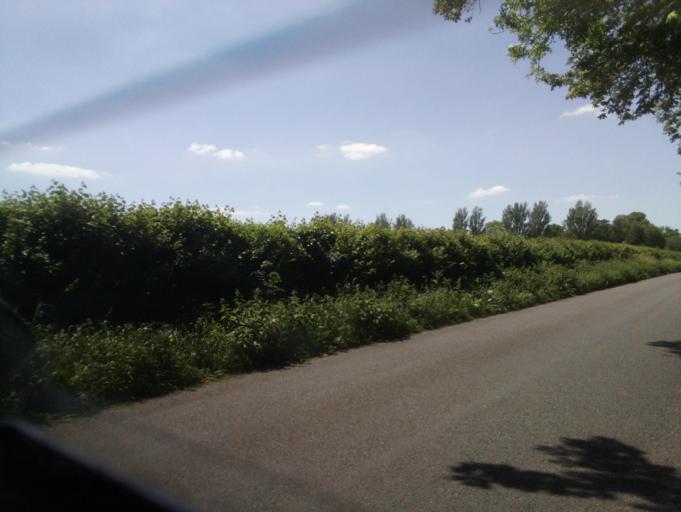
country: GB
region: England
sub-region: Wiltshire
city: Lyneham
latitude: 51.4724
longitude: -1.9740
